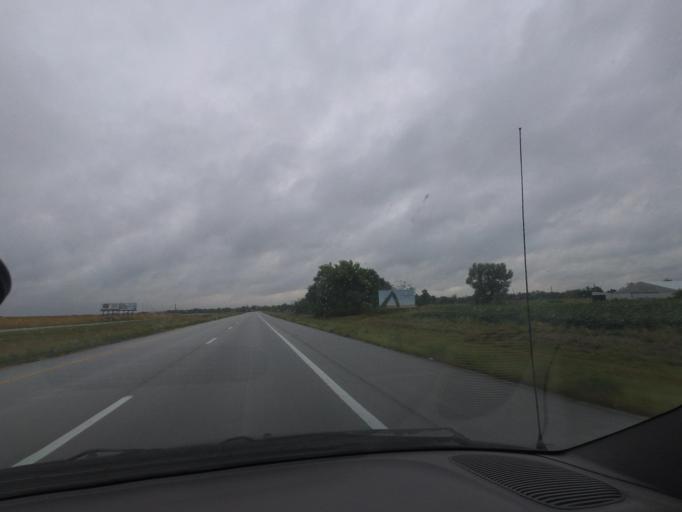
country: US
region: Missouri
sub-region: Marion County
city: Monroe City
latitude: 39.6646
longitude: -91.6821
